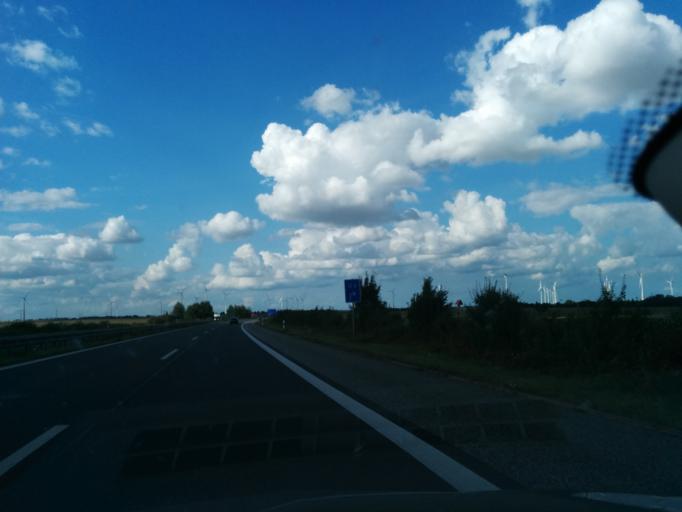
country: DE
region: Brandenburg
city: Schenkenberg
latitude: 53.3460
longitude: 13.9763
